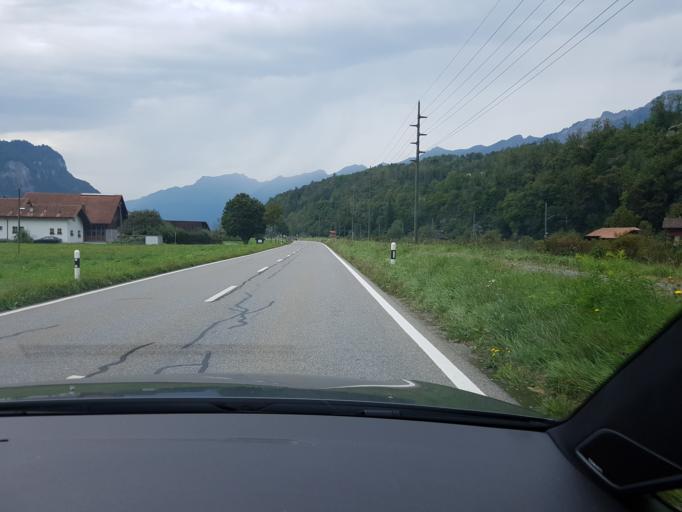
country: CH
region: Bern
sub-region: Interlaken-Oberhasli District
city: Brienz
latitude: 46.7460
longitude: 8.1050
